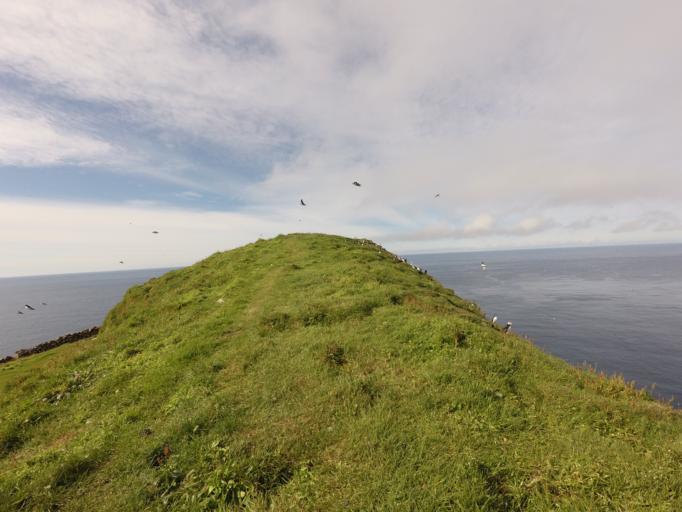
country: FO
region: Vagar
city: Sorvagur
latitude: 62.1044
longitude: -7.6529
